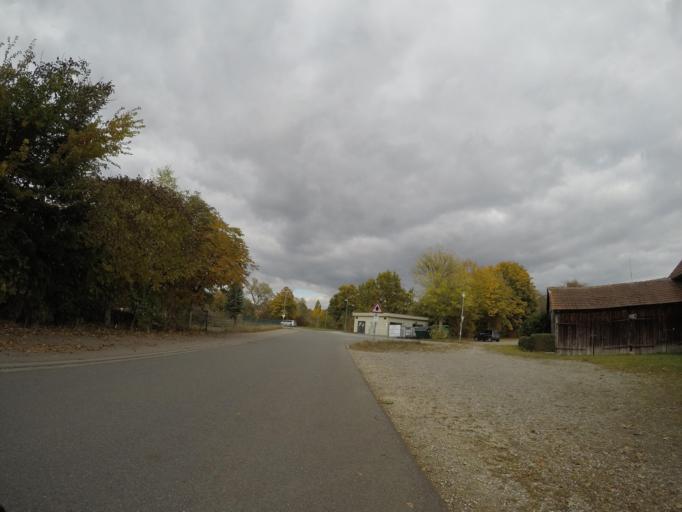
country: DE
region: Baden-Wuerttemberg
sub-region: Tuebingen Region
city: Munderkingen
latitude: 48.2334
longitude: 9.6492
